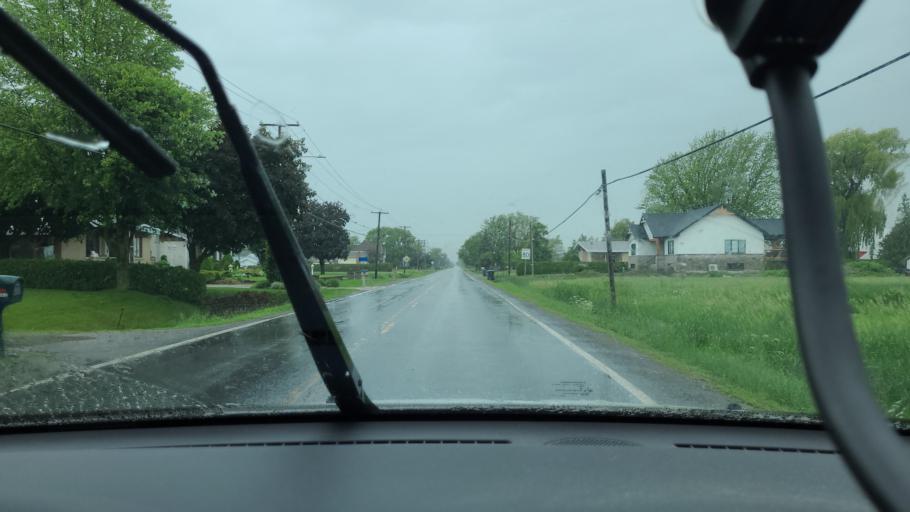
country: CA
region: Quebec
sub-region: Monteregie
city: Saint-Hyacinthe
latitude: 45.6173
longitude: -72.9996
